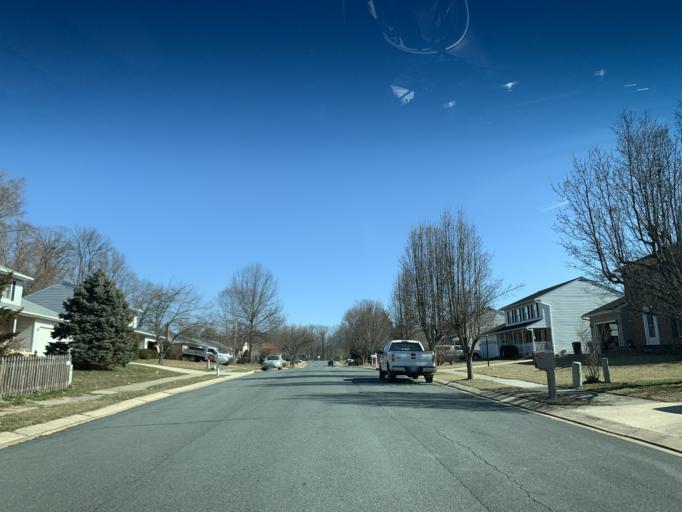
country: US
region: Maryland
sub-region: Harford County
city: South Bel Air
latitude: 39.5411
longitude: -76.2986
